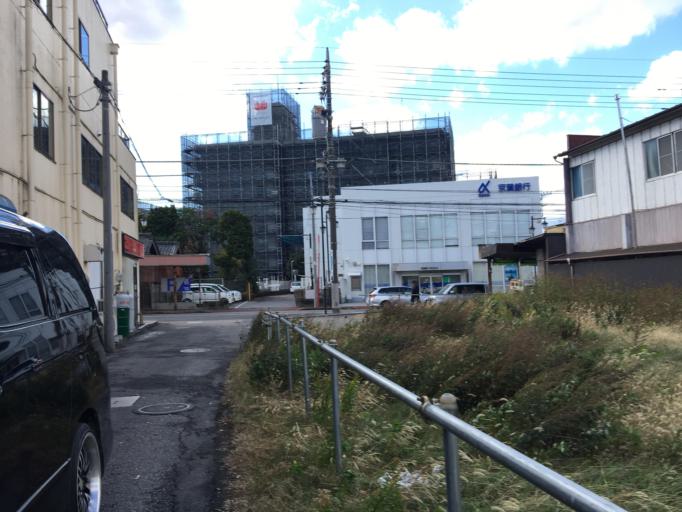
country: JP
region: Chiba
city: Noda
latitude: 35.9473
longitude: 139.8623
